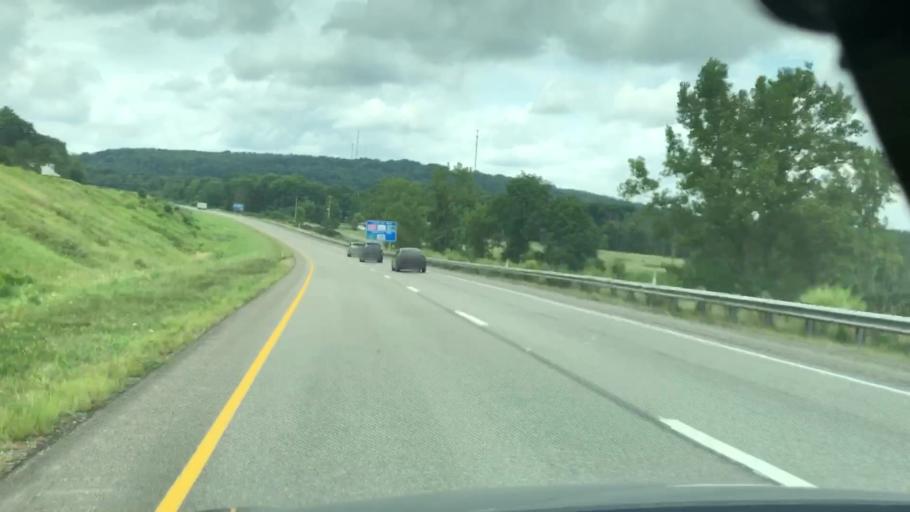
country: US
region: Pennsylvania
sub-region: Crawford County
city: Meadville
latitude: 41.6102
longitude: -80.1659
